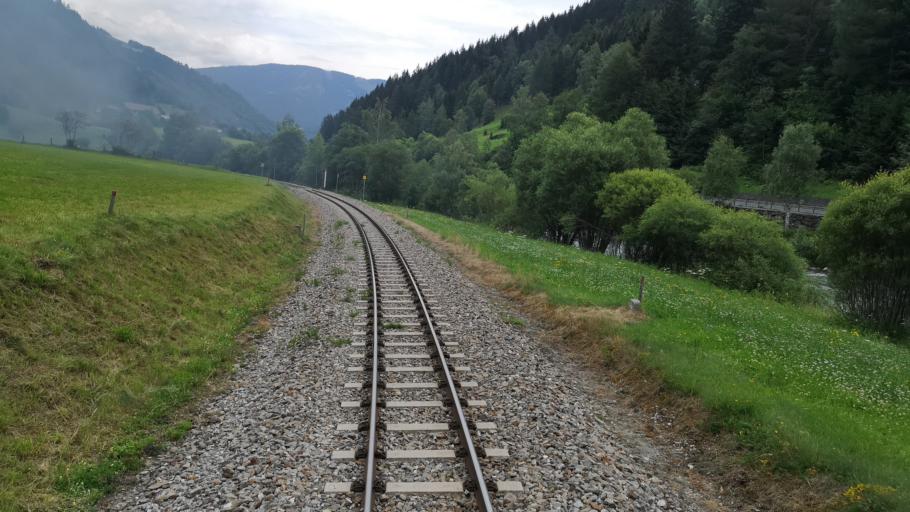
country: AT
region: Salzburg
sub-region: Politischer Bezirk Tamsweg
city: Ramingstein
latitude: 47.0737
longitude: 13.8551
